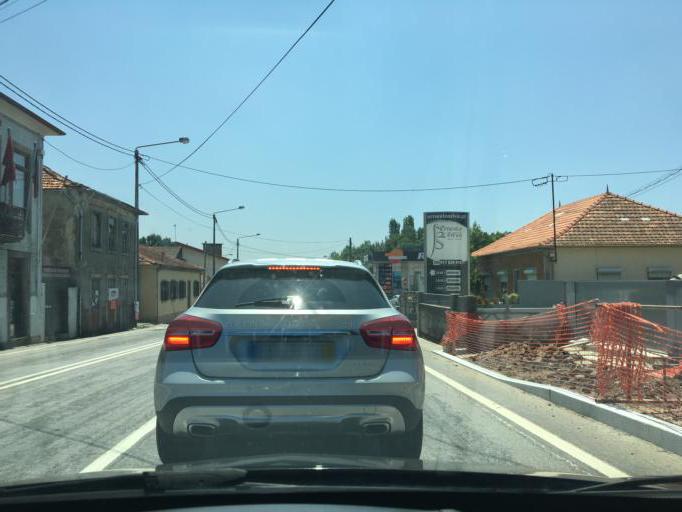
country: PT
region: Porto
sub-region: Maia
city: Gemunde
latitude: 41.2467
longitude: -8.6488
